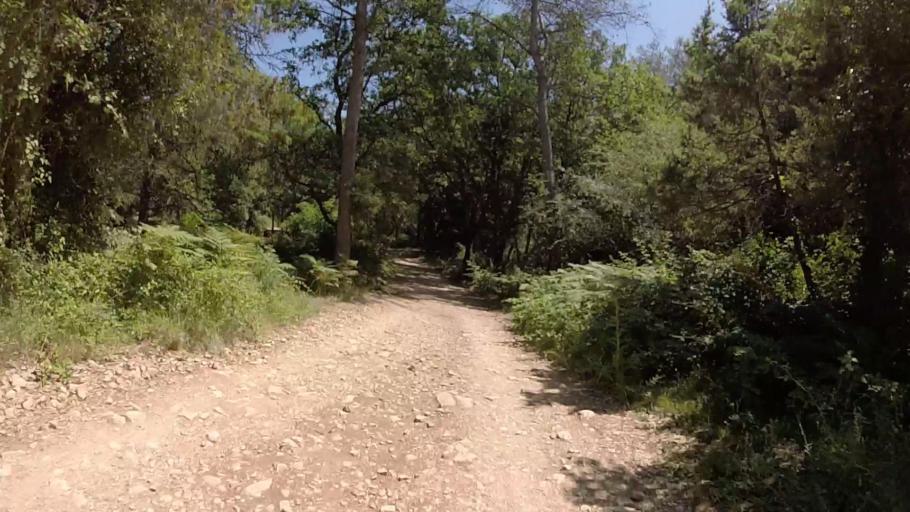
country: FR
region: Provence-Alpes-Cote d'Azur
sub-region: Departement des Alpes-Maritimes
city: Le Cannet
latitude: 43.5979
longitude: 7.0297
